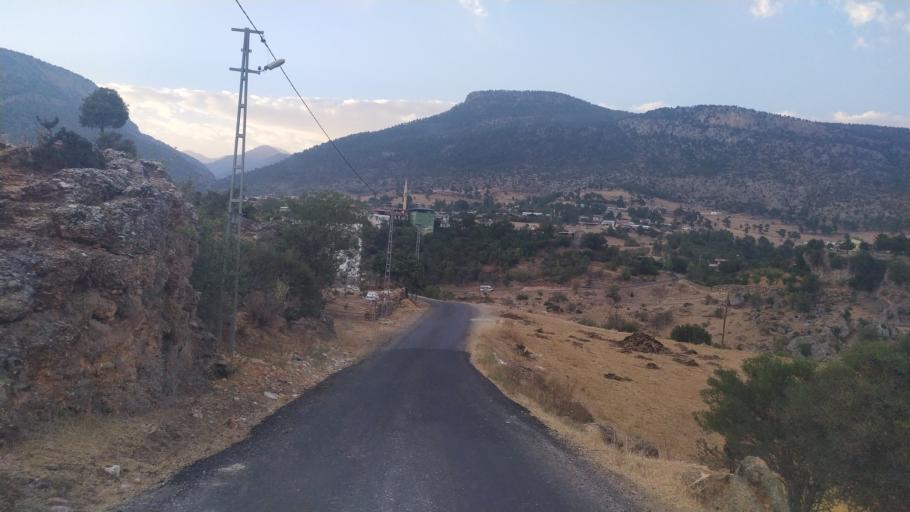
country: TR
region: Mersin
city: Camliyayla
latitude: 37.2358
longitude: 34.7180
